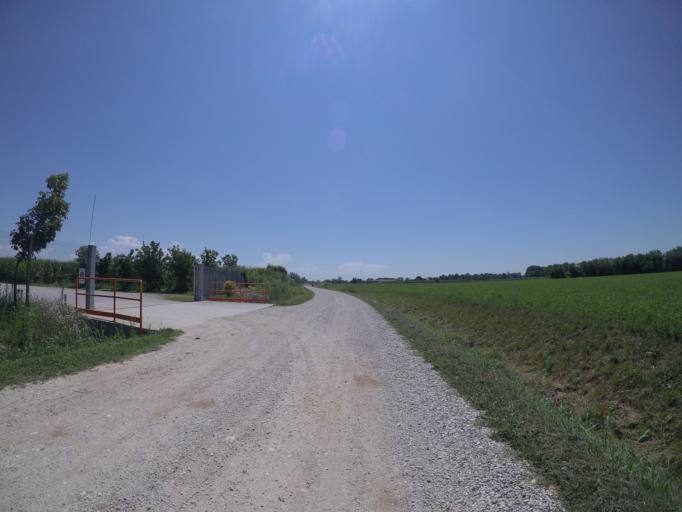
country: IT
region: Friuli Venezia Giulia
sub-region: Provincia di Udine
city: Talmassons
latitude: 45.9283
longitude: 13.1007
